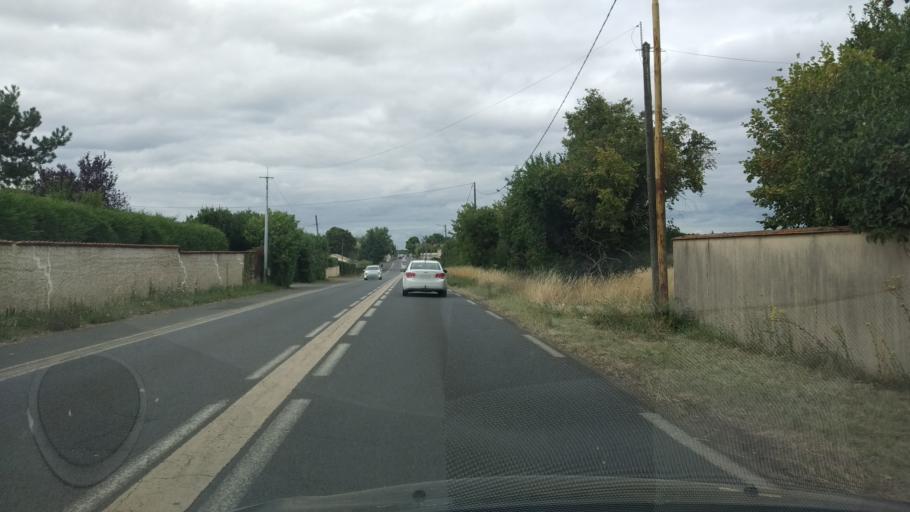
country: FR
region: Poitou-Charentes
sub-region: Departement de la Vienne
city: Smarves
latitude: 46.5113
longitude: 0.3594
